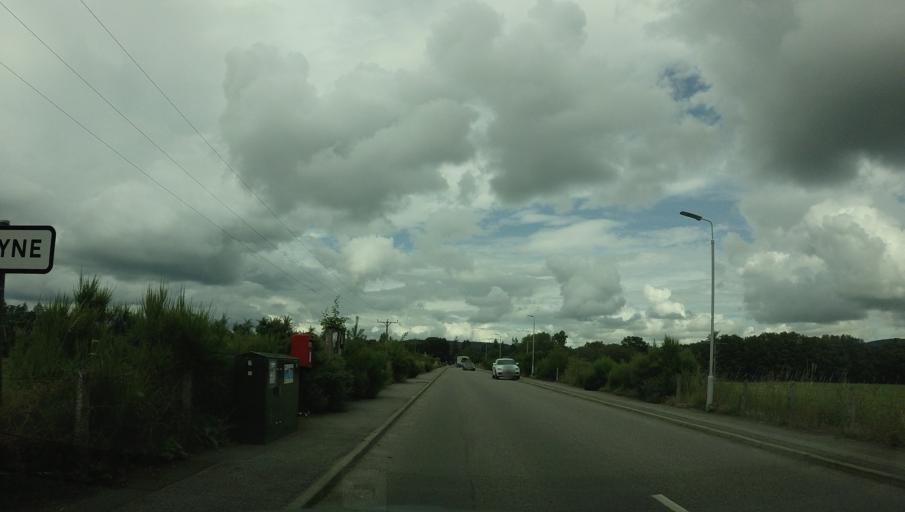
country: GB
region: Scotland
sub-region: Aberdeenshire
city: Aboyne
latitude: 57.0681
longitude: -2.7850
